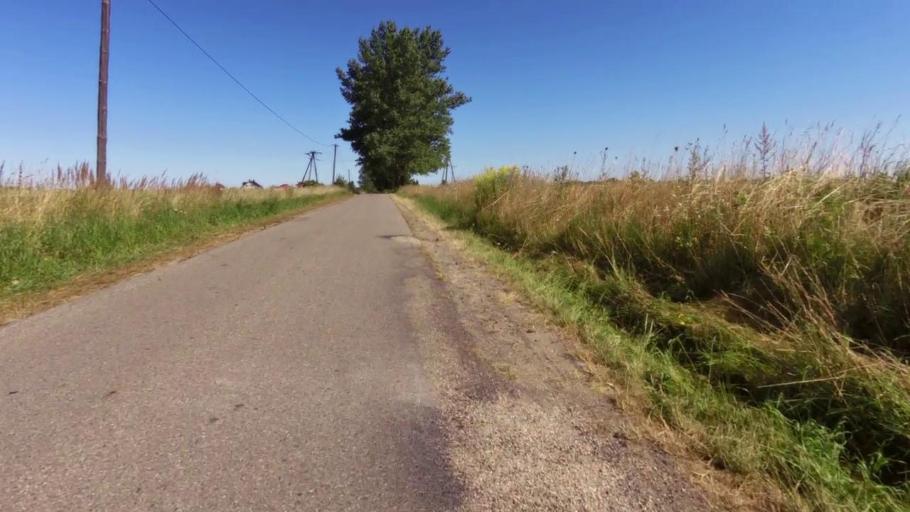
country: PL
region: West Pomeranian Voivodeship
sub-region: Powiat drawski
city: Czaplinek
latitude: 53.5500
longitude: 16.2189
